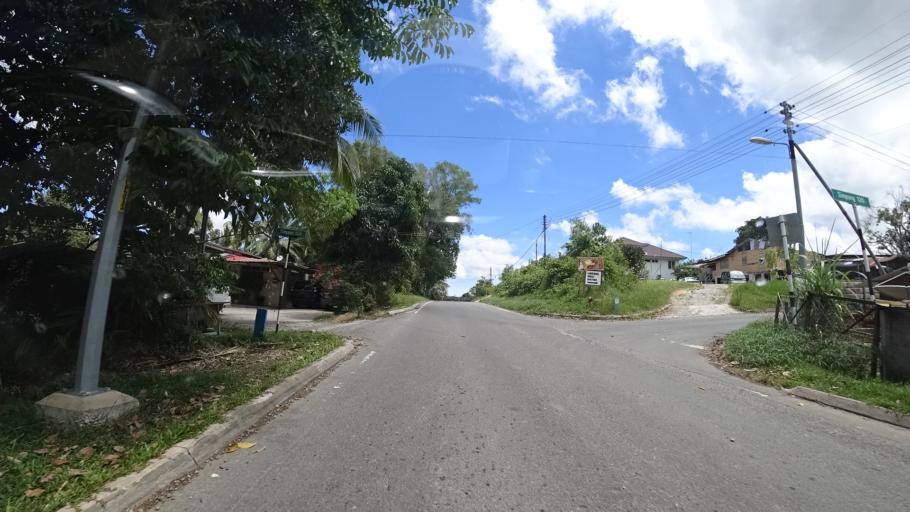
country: BN
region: Brunei and Muara
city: Bandar Seri Begawan
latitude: 4.9415
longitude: 114.9515
